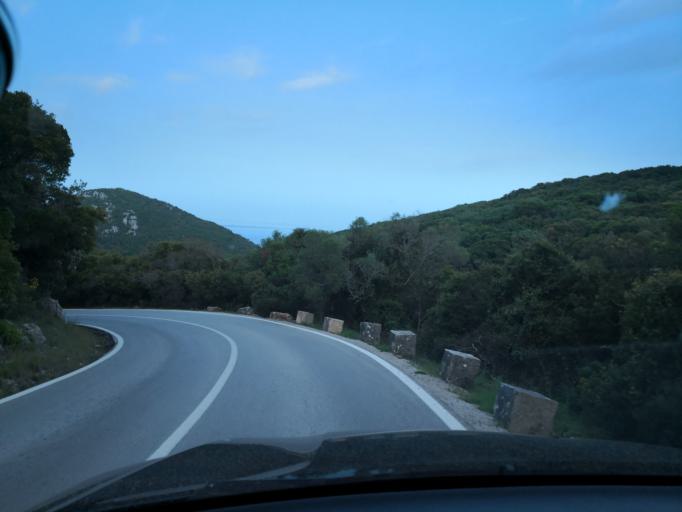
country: PT
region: Setubal
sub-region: Sesimbra
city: Sesimbra
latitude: 38.4614
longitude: -9.0069
